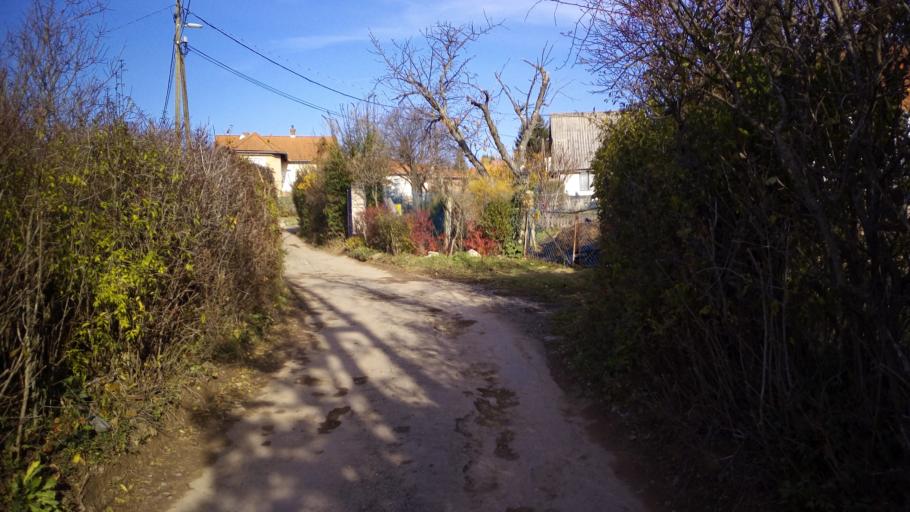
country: HU
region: Baranya
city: Pecs
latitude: 46.0905
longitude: 18.1833
